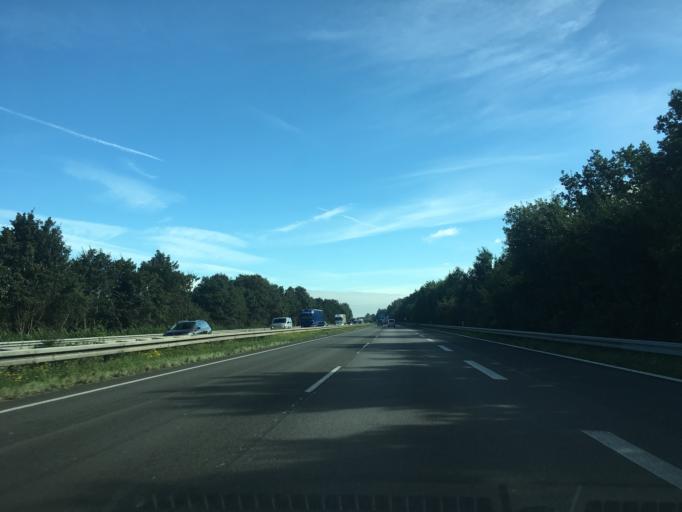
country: DE
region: North Rhine-Westphalia
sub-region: Regierungsbezirk Munster
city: Ladbergen
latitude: 52.1012
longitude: 7.6782
